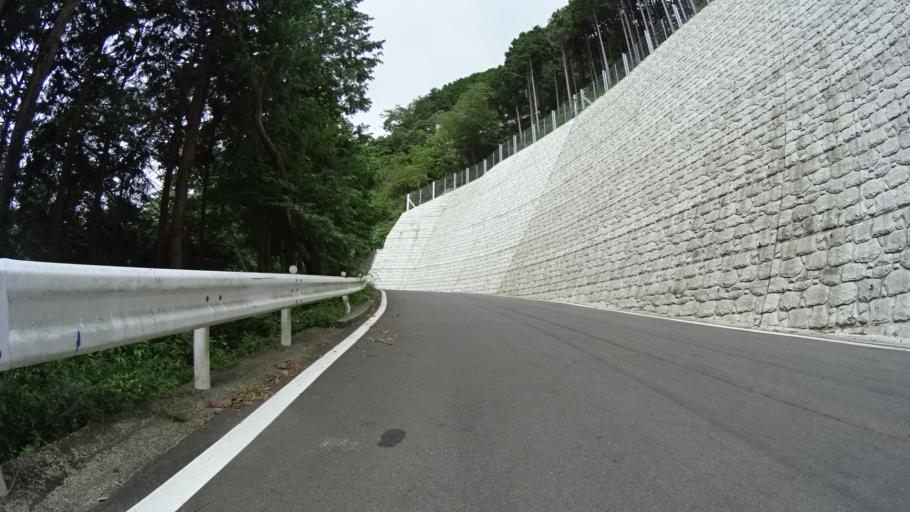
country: JP
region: Kanagawa
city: Hadano
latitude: 35.4098
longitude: 139.2121
